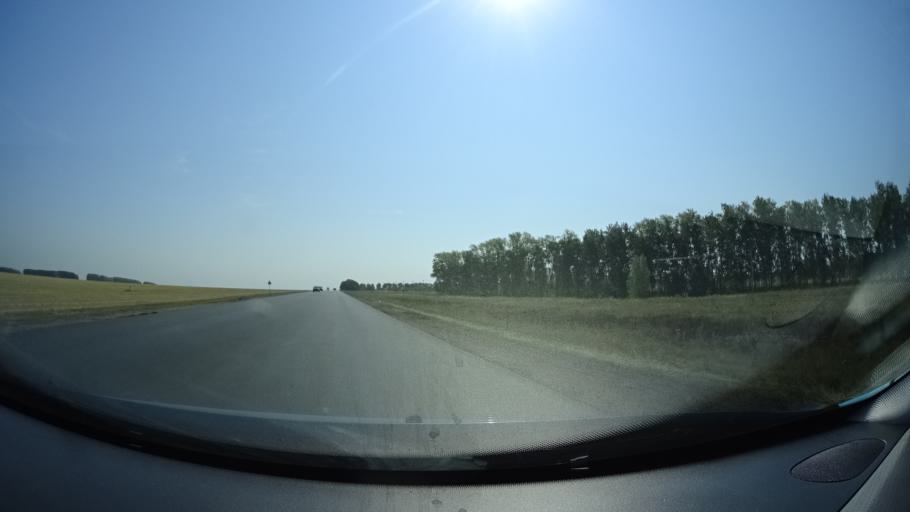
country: RU
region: Bashkortostan
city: Kabakovo
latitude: 54.4797
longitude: 55.9277
